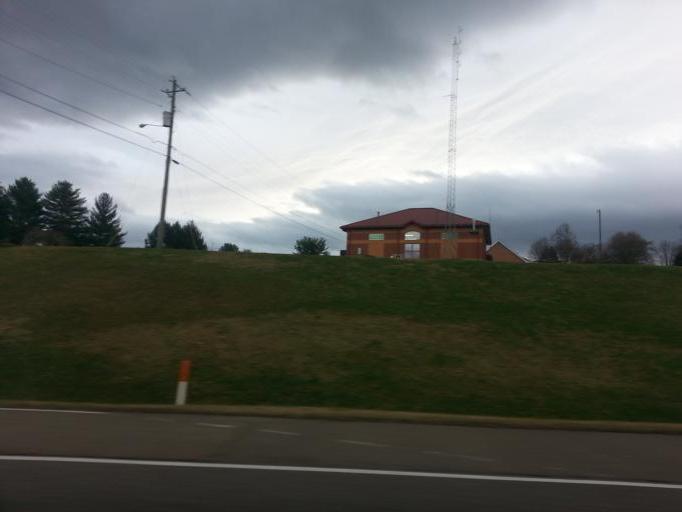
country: US
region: Tennessee
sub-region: Carter County
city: Central
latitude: 36.3224
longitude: -82.2729
